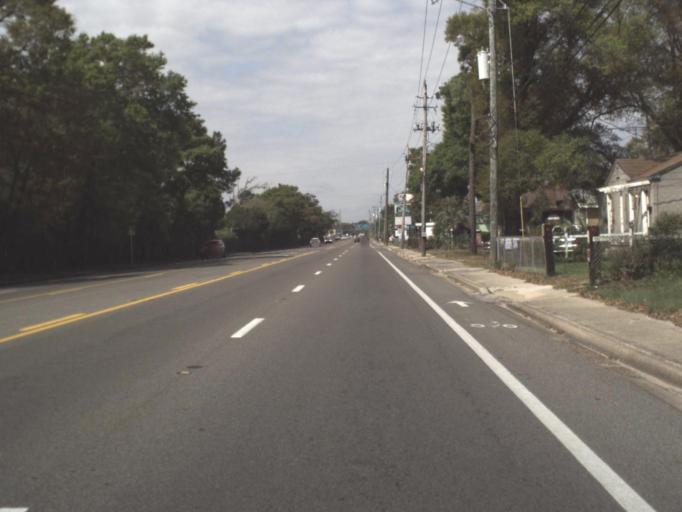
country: US
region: Florida
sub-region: Escambia County
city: Warrington
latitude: 30.3903
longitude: -87.2680
